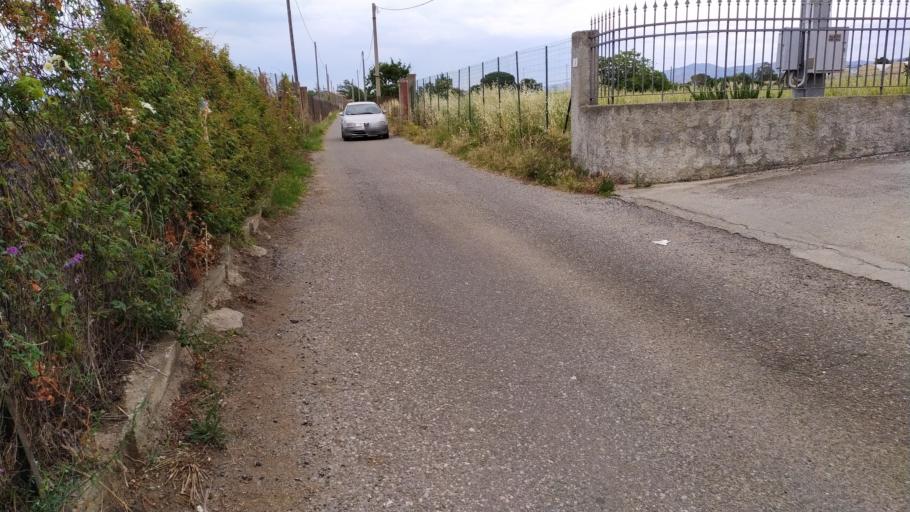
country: IT
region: Sicily
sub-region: Messina
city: Meri
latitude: 38.1862
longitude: 15.2543
